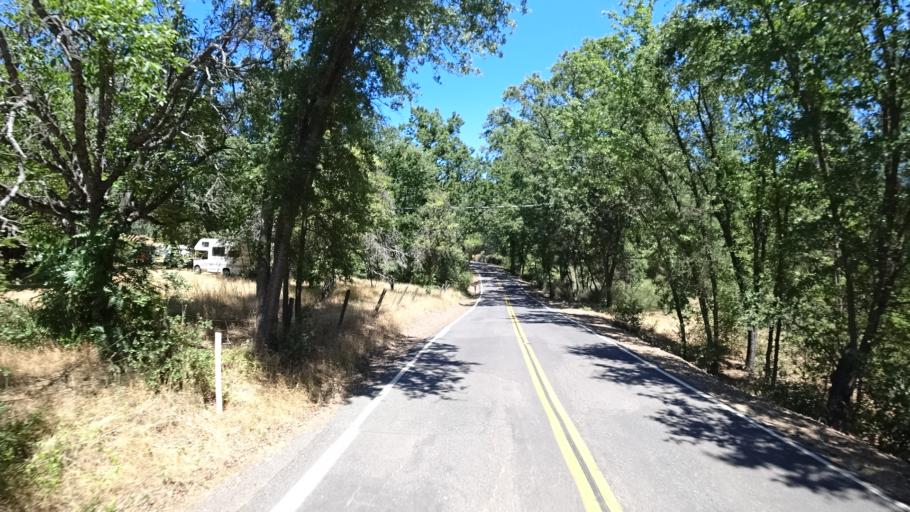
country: US
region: California
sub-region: Calaveras County
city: Murphys
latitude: 38.1293
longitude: -120.5009
